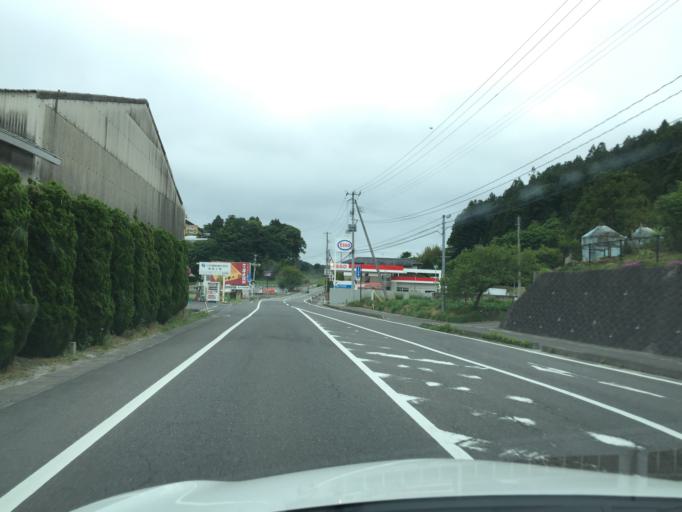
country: JP
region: Fukushima
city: Funehikimachi-funehiki
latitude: 37.3320
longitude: 140.6567
